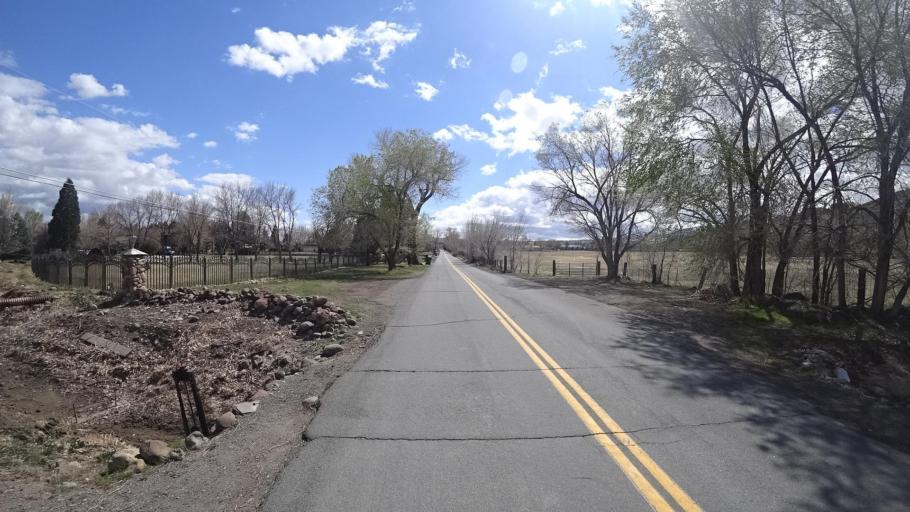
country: US
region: Nevada
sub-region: Washoe County
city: Reno
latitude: 39.4371
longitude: -119.7893
